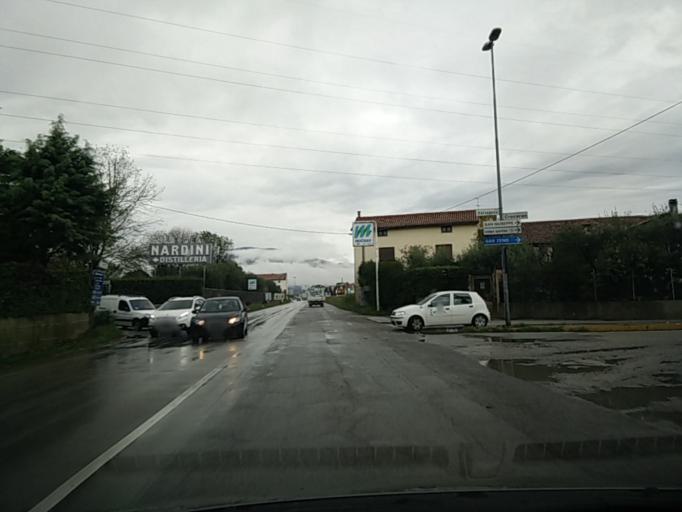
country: IT
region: Veneto
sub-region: Provincia di Vicenza
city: San Zeno-San Giuseppe
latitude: 45.7406
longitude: 11.7571
